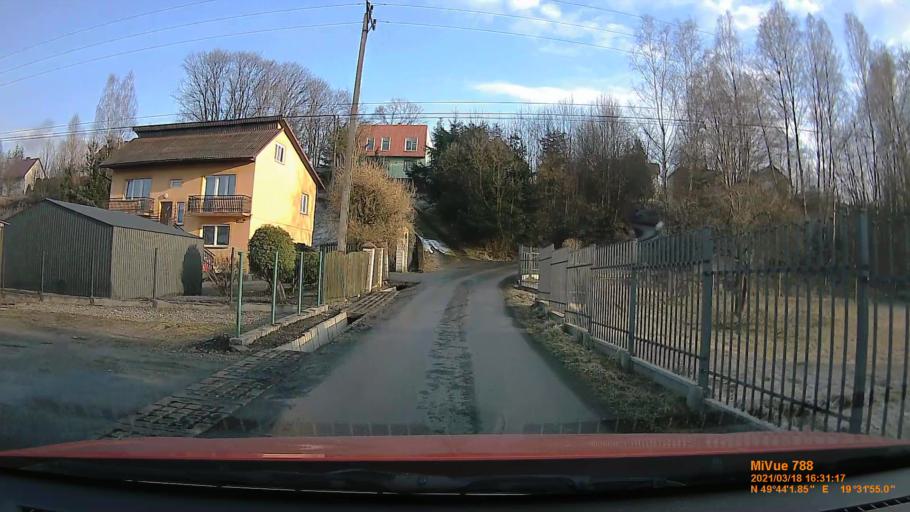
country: PL
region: Lesser Poland Voivodeship
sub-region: Powiat suski
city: Stryszawa
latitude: 49.7338
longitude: 19.5320
